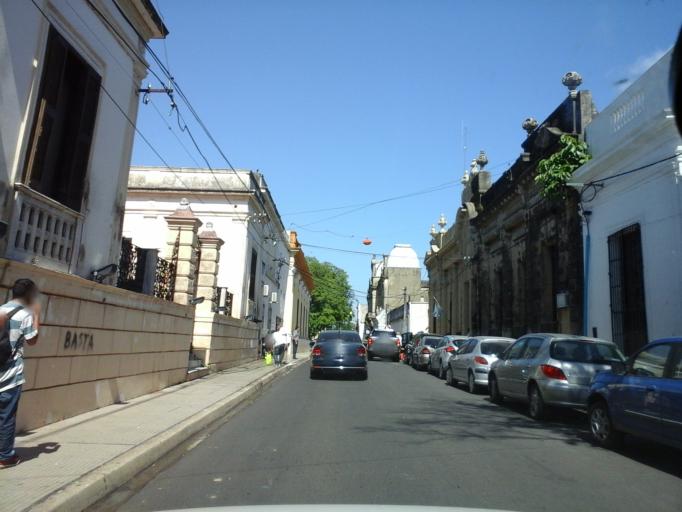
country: AR
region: Corrientes
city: Corrientes
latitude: -27.4629
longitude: -58.8380
